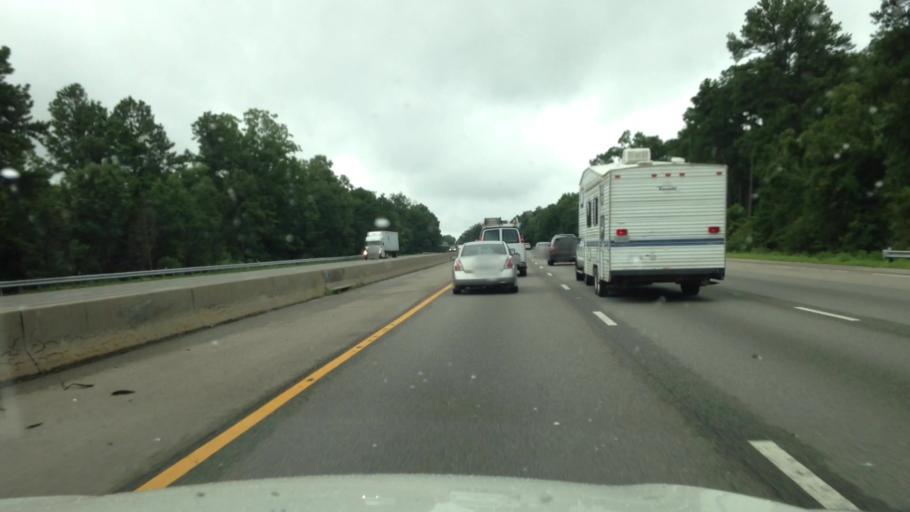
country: US
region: Virginia
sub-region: Chesterfield County
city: Chester
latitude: 37.3482
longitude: -77.4055
